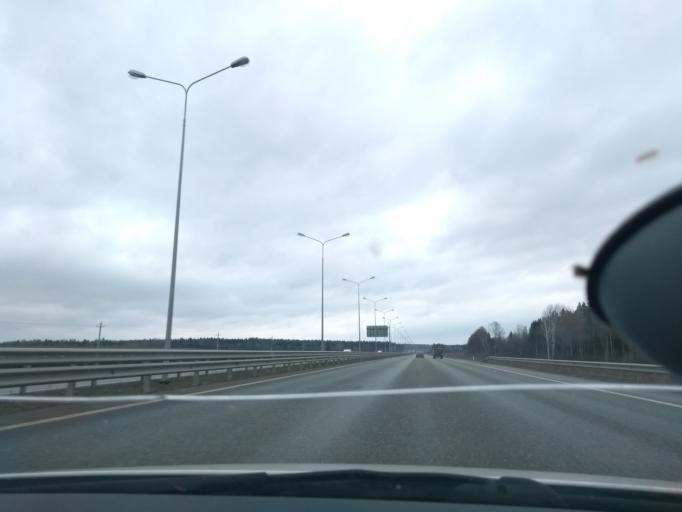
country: RU
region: Perm
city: Bershet'
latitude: 57.6864
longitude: 56.4144
